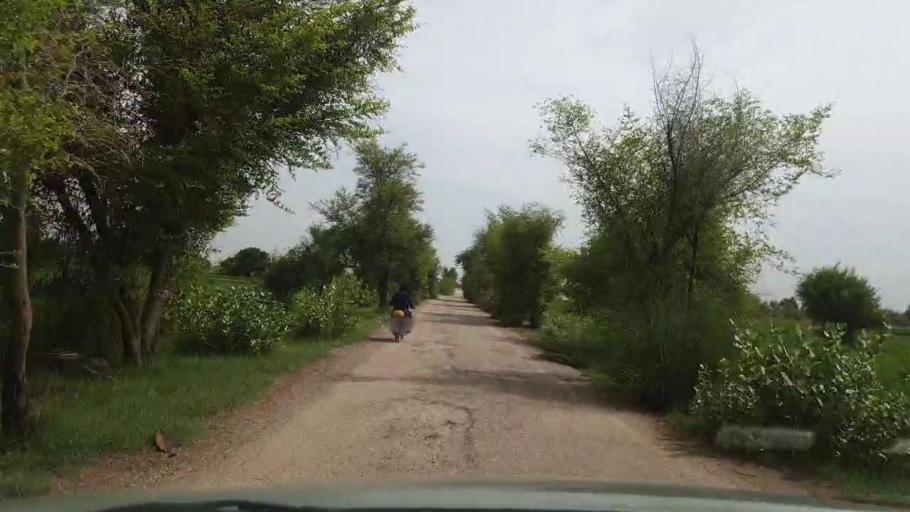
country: PK
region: Sindh
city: Kot Diji
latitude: 27.1063
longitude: 69.0210
